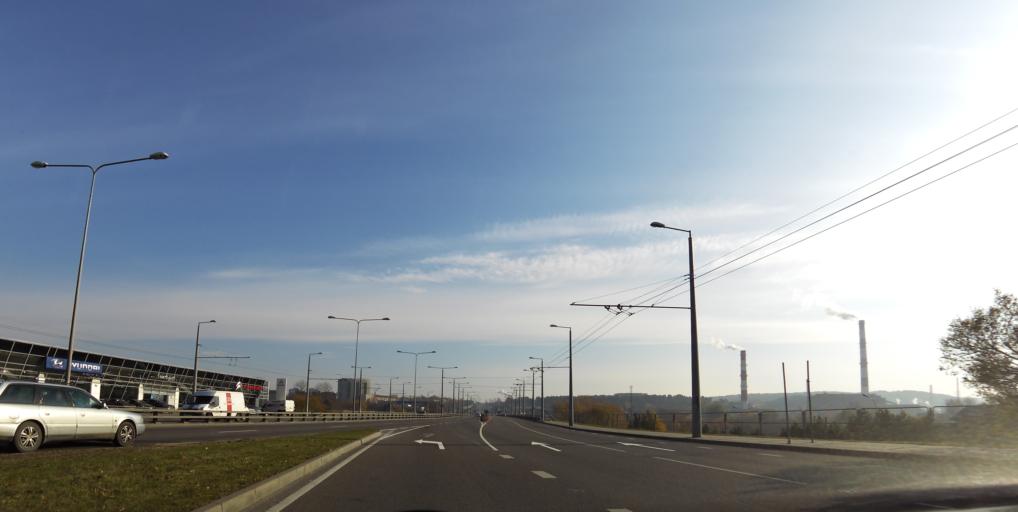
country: LT
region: Vilnius County
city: Lazdynai
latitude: 54.6710
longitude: 25.2265
